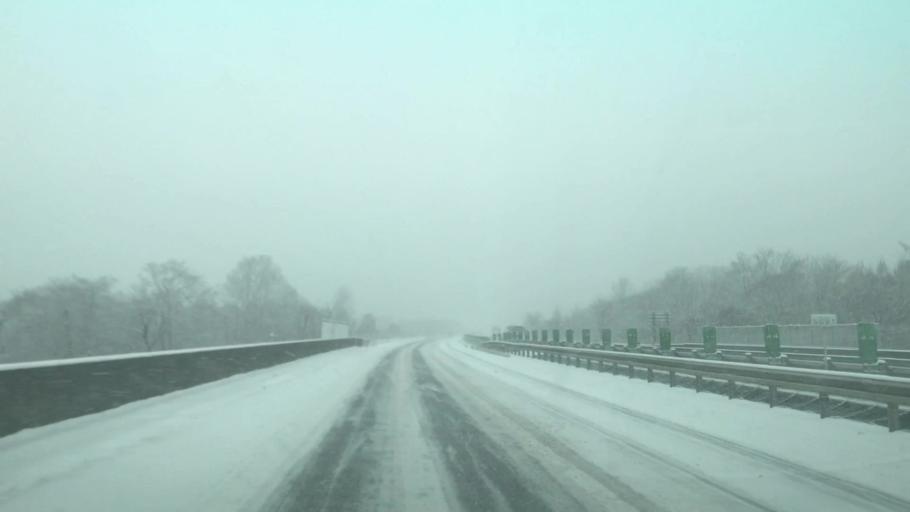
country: JP
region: Hokkaido
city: Shiraoi
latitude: 42.5104
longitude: 141.2699
